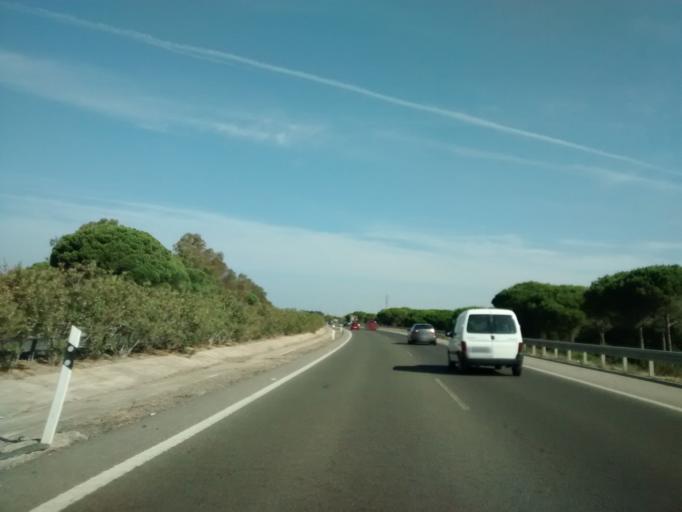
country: ES
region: Andalusia
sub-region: Provincia de Cadiz
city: Chiclana de la Frontera
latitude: 36.3811
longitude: -6.1147
